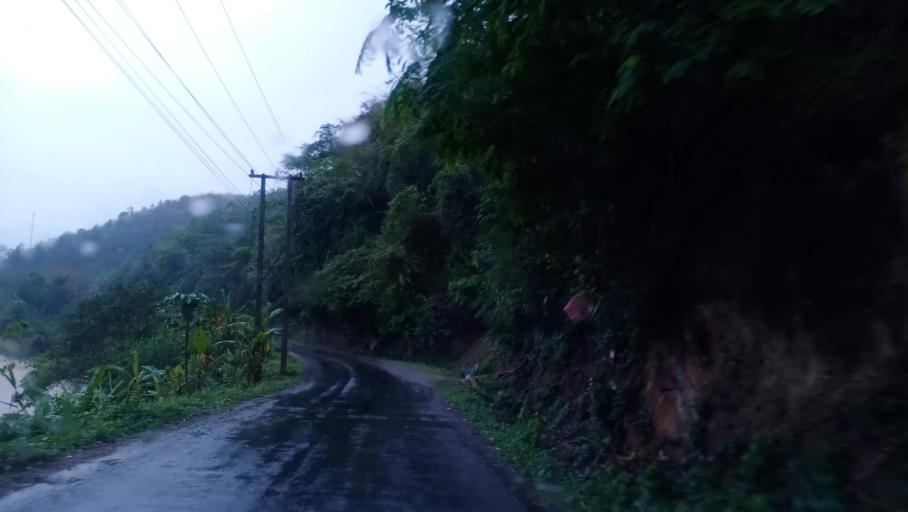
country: LA
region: Phongsali
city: Khoa
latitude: 21.0617
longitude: 102.4700
